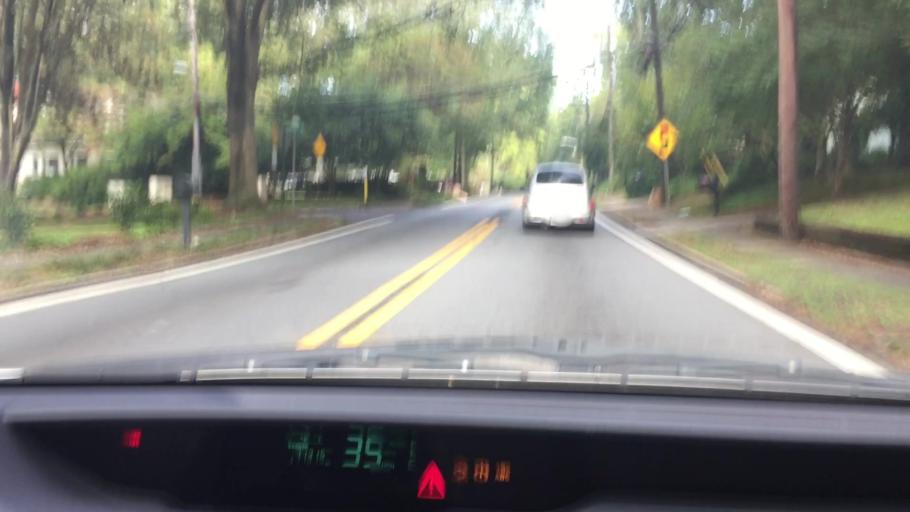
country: US
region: Georgia
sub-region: DeKalb County
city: Decatur
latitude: 33.7595
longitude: -84.2916
